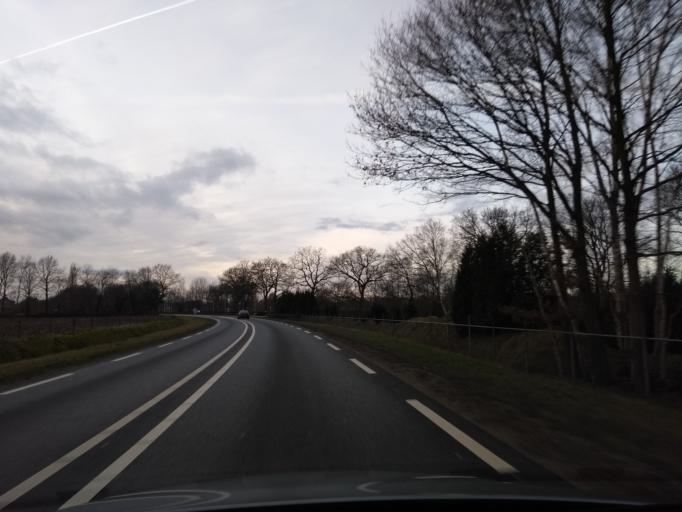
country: NL
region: Overijssel
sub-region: Gemeente Tubbergen
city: Tubbergen
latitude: 52.3647
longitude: 6.8408
